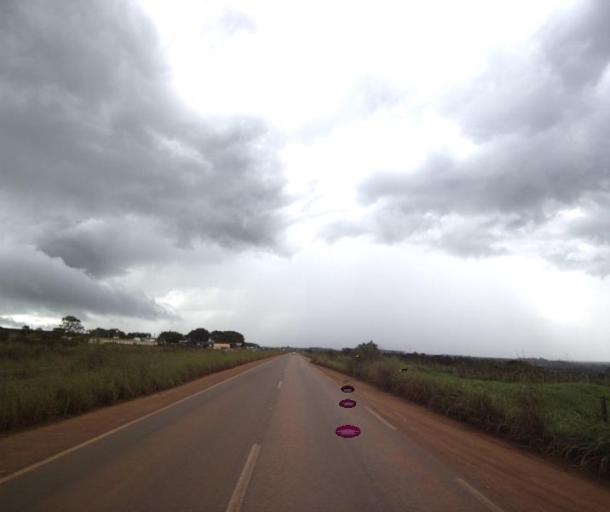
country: BR
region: Goias
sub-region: Anapolis
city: Anapolis
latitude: -16.2571
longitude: -48.9895
